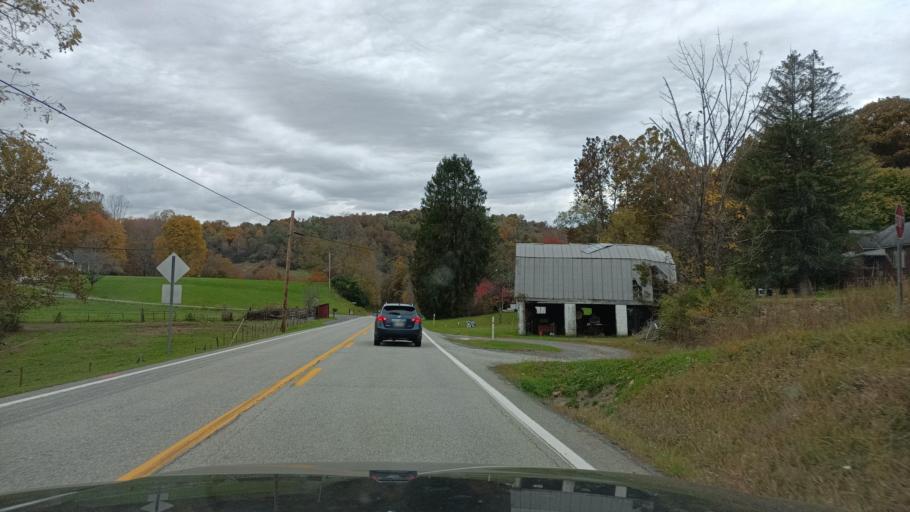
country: US
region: West Virginia
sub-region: Taylor County
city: Grafton
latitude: 39.3423
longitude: -79.9622
